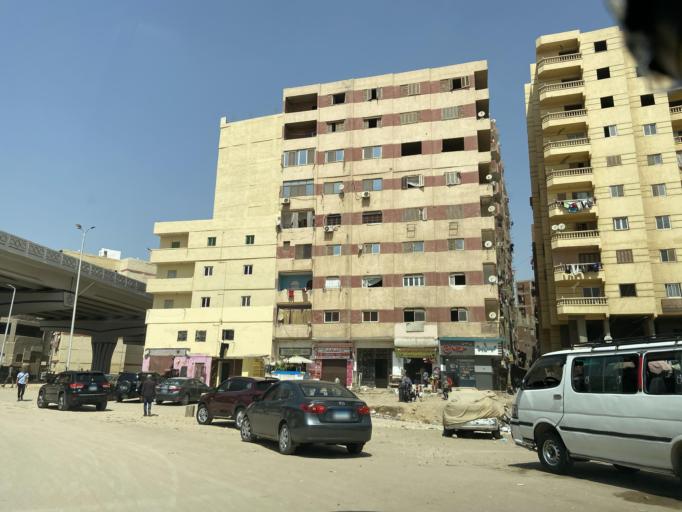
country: EG
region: Muhafazat al Qahirah
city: Cairo
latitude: 30.0620
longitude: 31.3800
